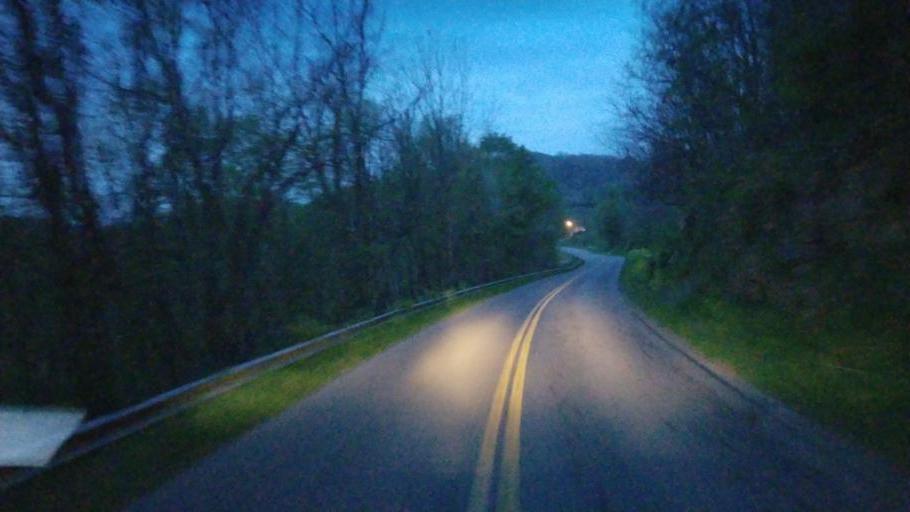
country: US
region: Virginia
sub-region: Smyth County
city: Atkins
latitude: 36.8519
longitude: -81.4662
